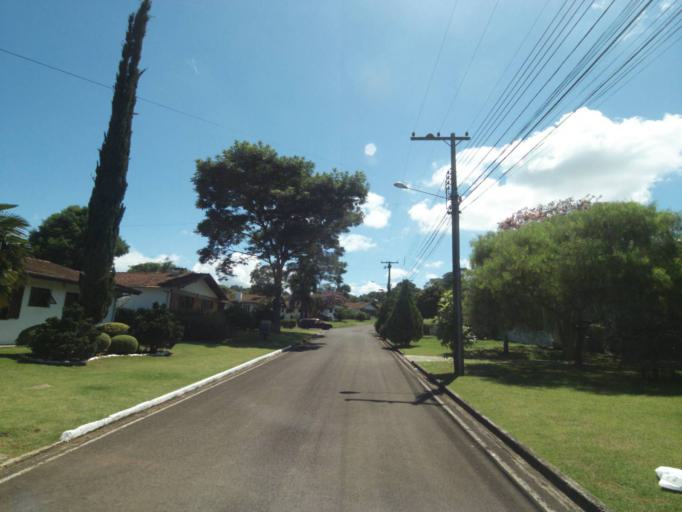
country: BR
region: Parana
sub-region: Chopinzinho
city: Chopinzinho
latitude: -25.7986
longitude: -52.0958
